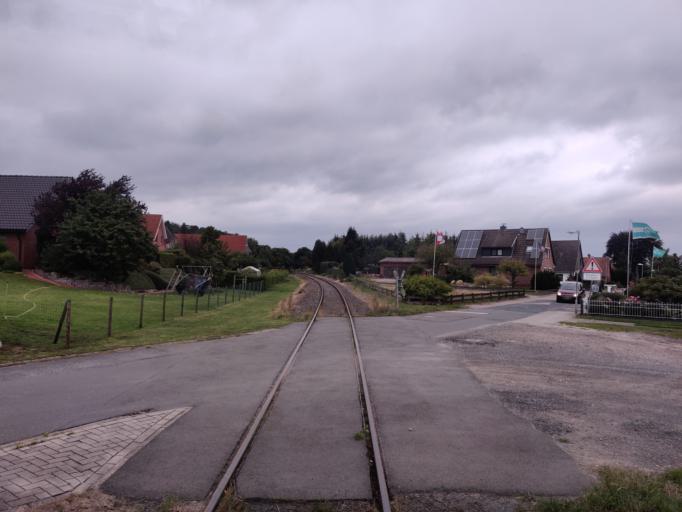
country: DE
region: Lower Saxony
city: Gnarrenburg
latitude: 53.3936
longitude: 9.0154
